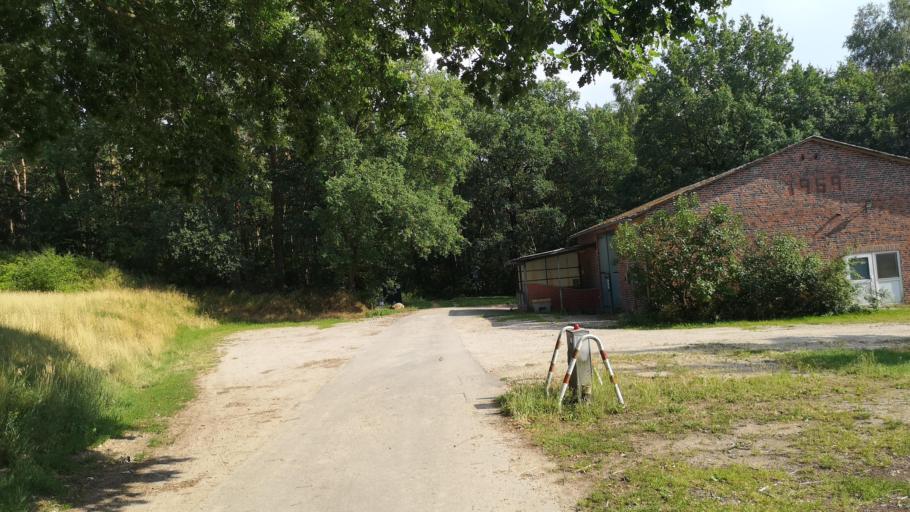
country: DE
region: Lower Saxony
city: Dahlenburg
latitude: 53.2165
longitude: 10.7136
